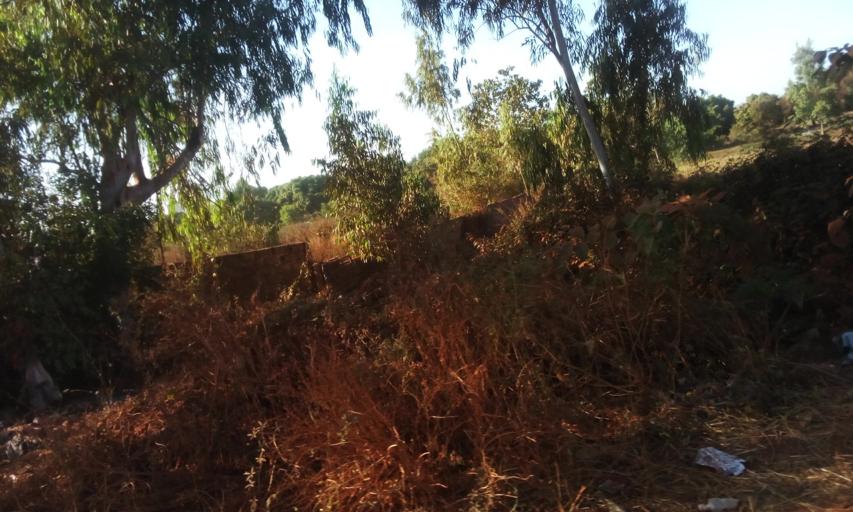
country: ML
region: Bamako
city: Bamako
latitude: 12.6400
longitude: -7.9110
